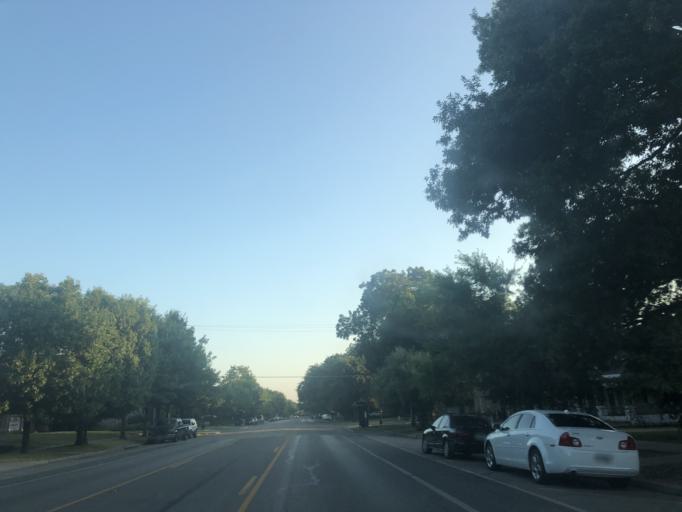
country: US
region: Texas
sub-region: Dallas County
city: Dallas
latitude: 32.7514
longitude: -96.8278
